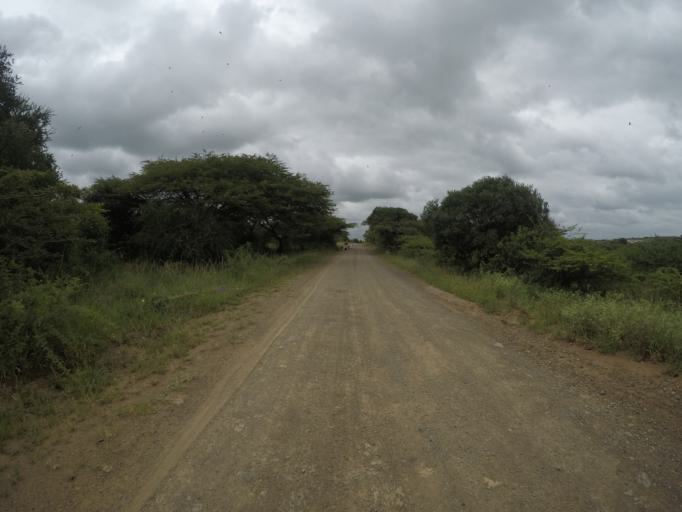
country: ZA
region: KwaZulu-Natal
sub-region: uThungulu District Municipality
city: Empangeni
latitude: -28.5604
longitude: 31.8760
